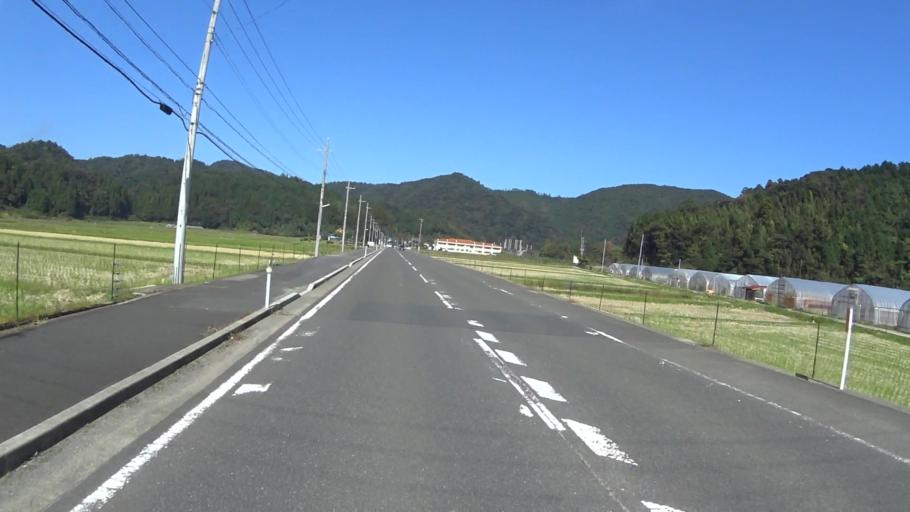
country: JP
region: Kyoto
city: Miyazu
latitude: 35.7239
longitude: 135.2547
